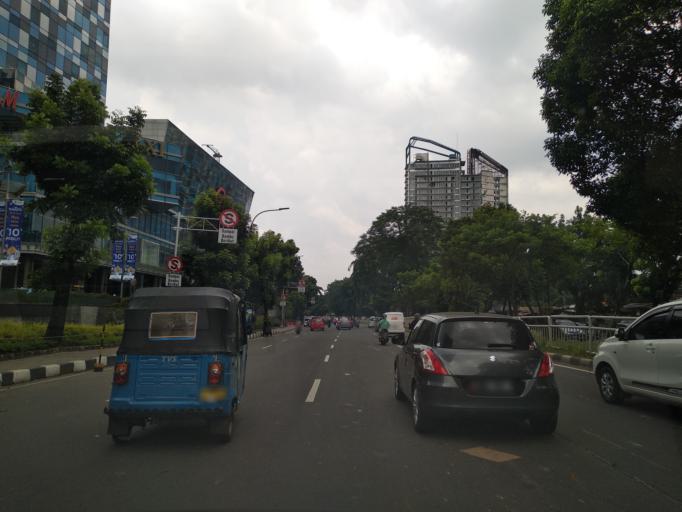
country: ID
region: Jakarta Raya
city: Jakarta
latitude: -6.2247
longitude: 106.8423
